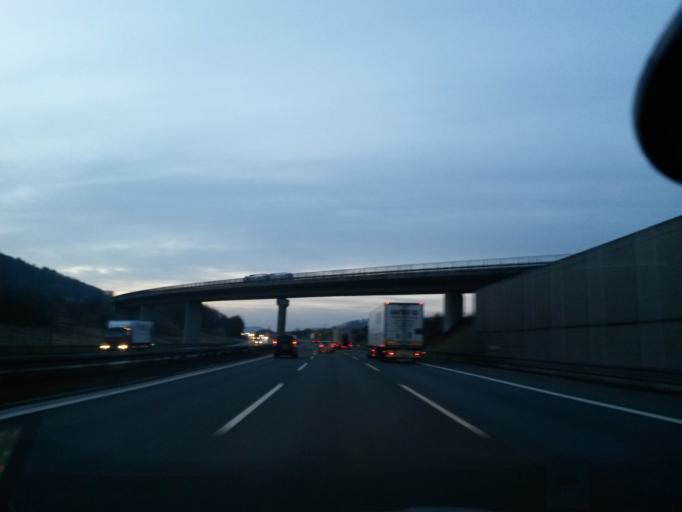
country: DE
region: Bavaria
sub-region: Regierungsbezirk Mittelfranken
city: Greding
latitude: 49.0755
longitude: 11.2954
